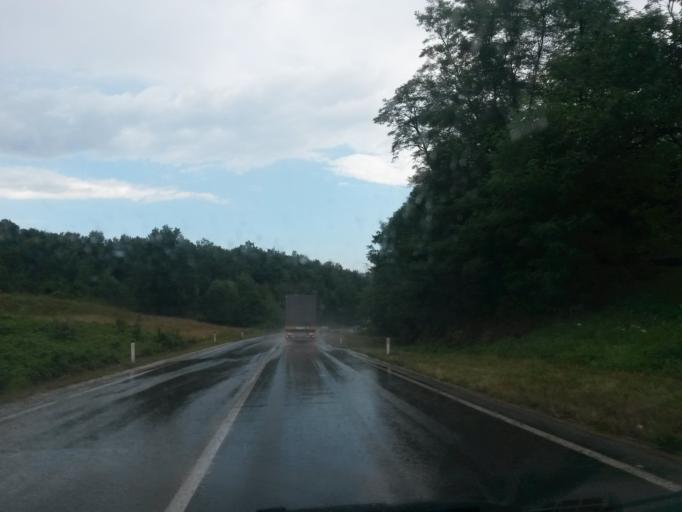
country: BA
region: Federation of Bosnia and Herzegovina
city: Lijesnica
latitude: 44.4664
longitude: 18.0661
